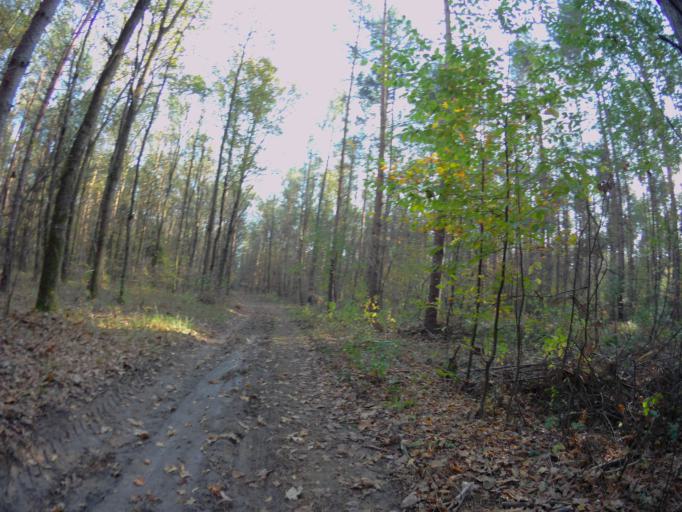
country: PL
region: Subcarpathian Voivodeship
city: Nowa Sarzyna
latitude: 50.3091
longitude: 22.3505
